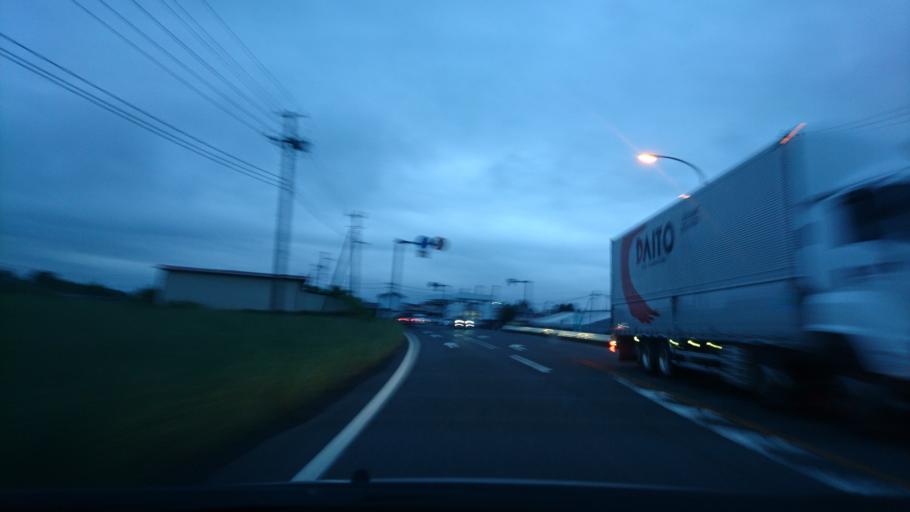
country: JP
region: Iwate
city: Ichinoseki
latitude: 38.8174
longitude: 141.0767
